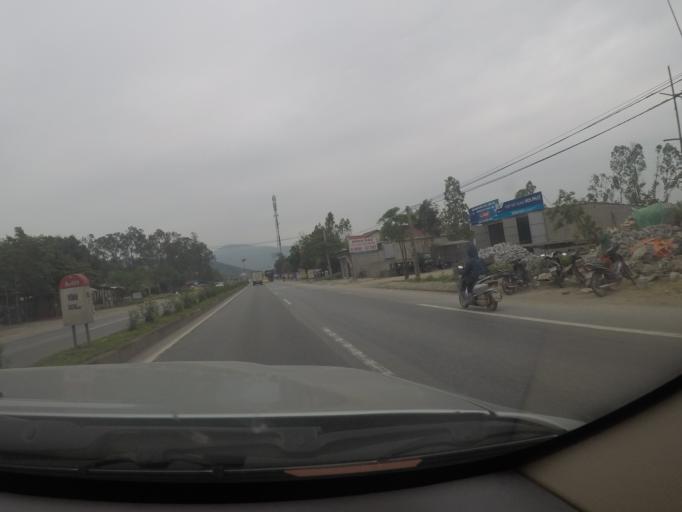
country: VN
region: Nghe An
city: Dien Chau
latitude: 18.9064
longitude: 105.6048
